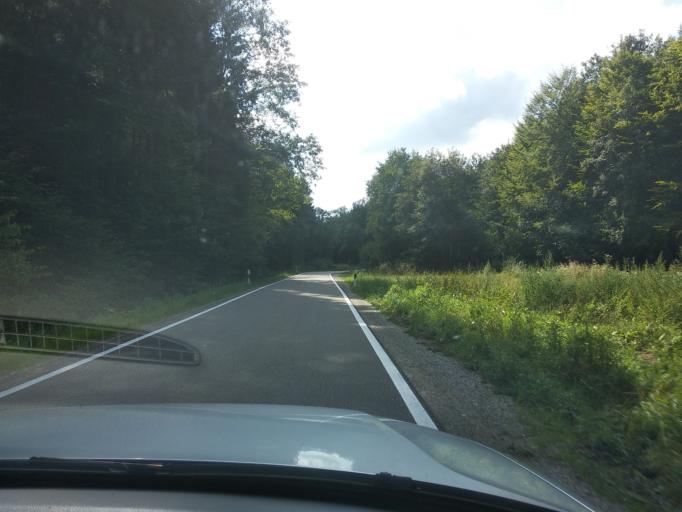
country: DE
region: Baden-Wuerttemberg
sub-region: Tuebingen Region
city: Aichstetten
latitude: 47.9052
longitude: 10.0478
